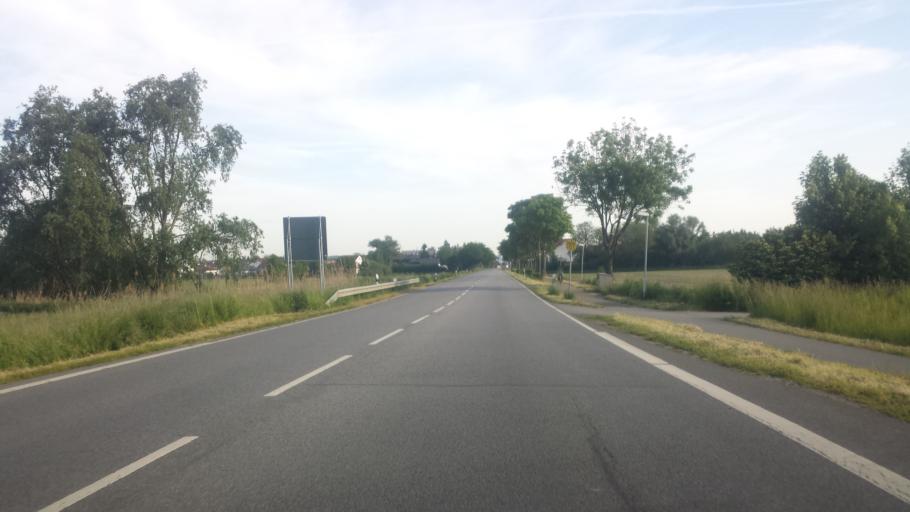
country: DE
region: Hesse
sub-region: Regierungsbezirk Darmstadt
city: Burstadt
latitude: 49.6567
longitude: 8.4507
